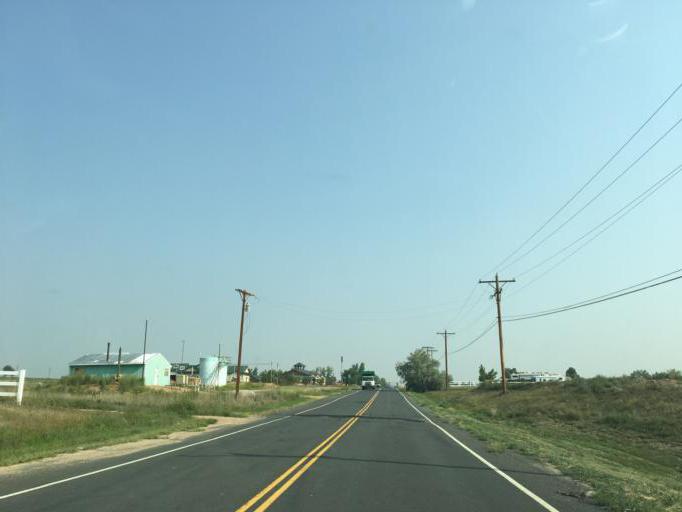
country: US
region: Colorado
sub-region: Adams County
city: Todd Creek
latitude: 39.9825
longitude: -104.8655
